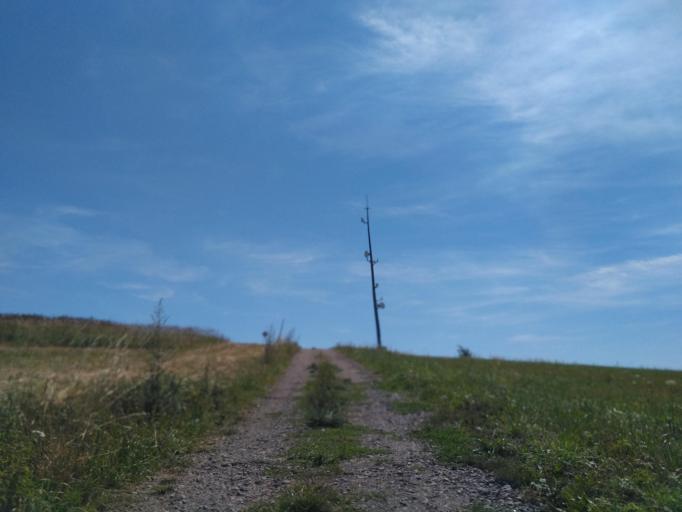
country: PL
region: Subcarpathian Voivodeship
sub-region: Powiat sanocki
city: Bukowsko
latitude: 49.4876
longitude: 22.0754
